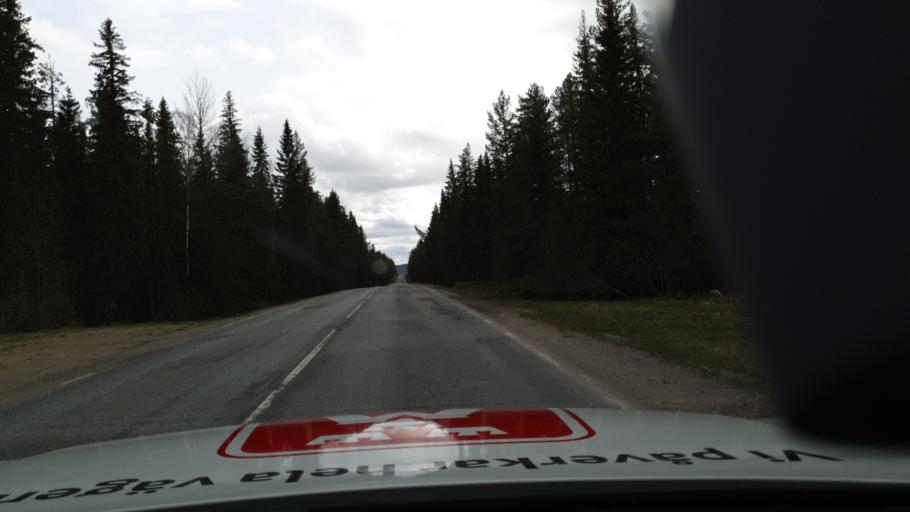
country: SE
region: Jaemtland
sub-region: Braecke Kommun
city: Braecke
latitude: 62.7785
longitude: 15.4629
